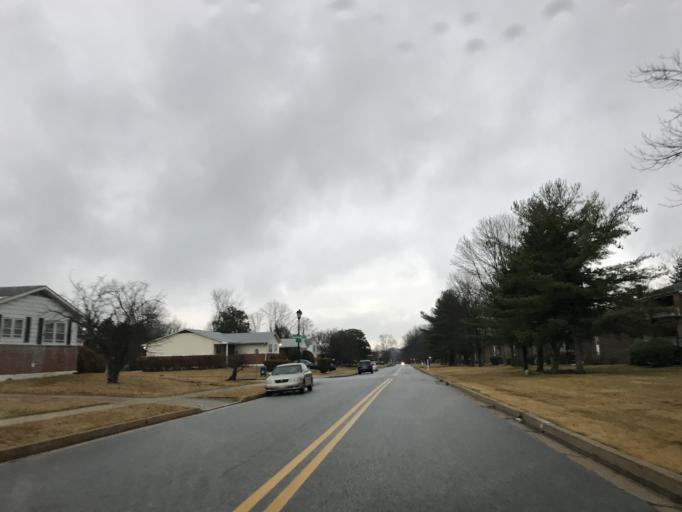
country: US
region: Maryland
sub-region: Baltimore County
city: Pikesville
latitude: 39.3720
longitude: -76.6896
